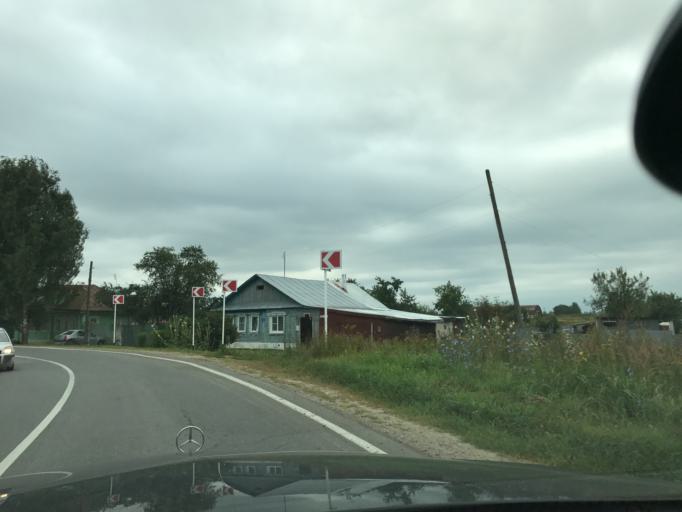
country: RU
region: Vladimir
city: Galitsy
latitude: 56.1751
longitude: 42.7962
